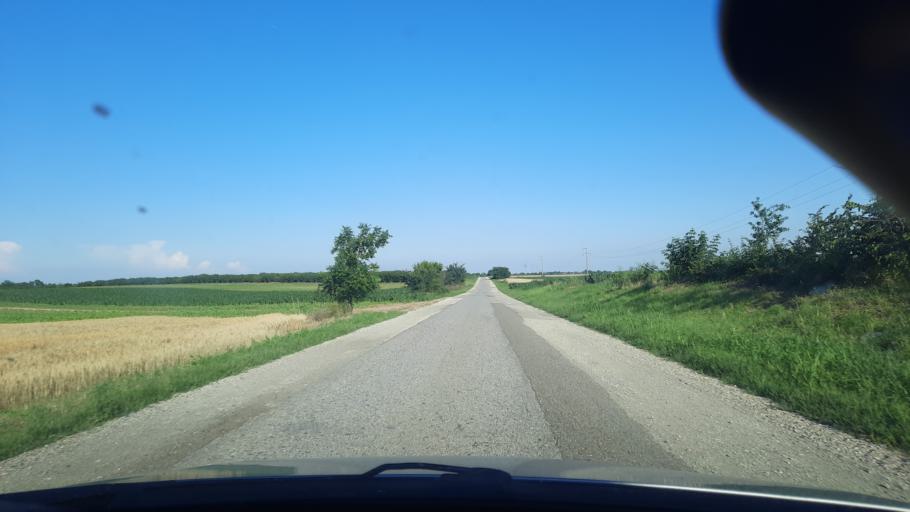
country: RS
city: Cortanovci
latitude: 45.1126
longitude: 19.9674
